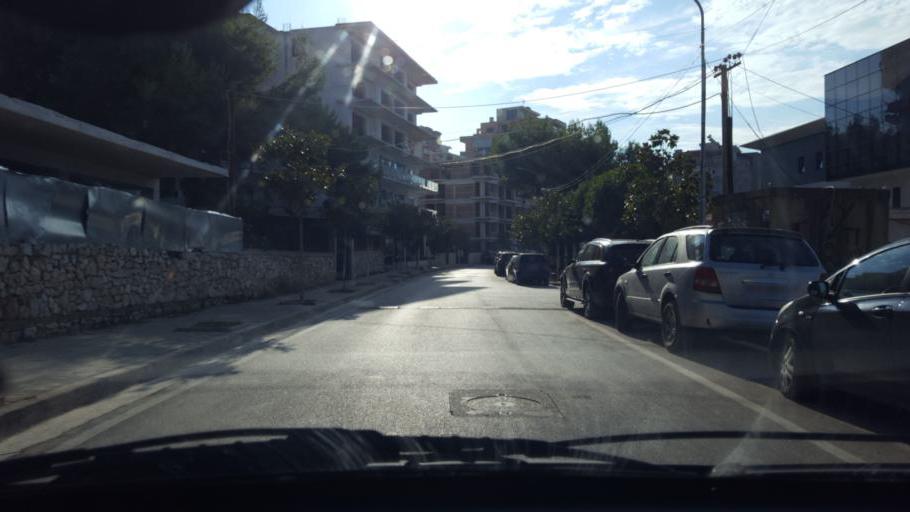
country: AL
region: Vlore
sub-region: Rrethi i Sarandes
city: Sarande
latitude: 39.8709
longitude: 19.9969
